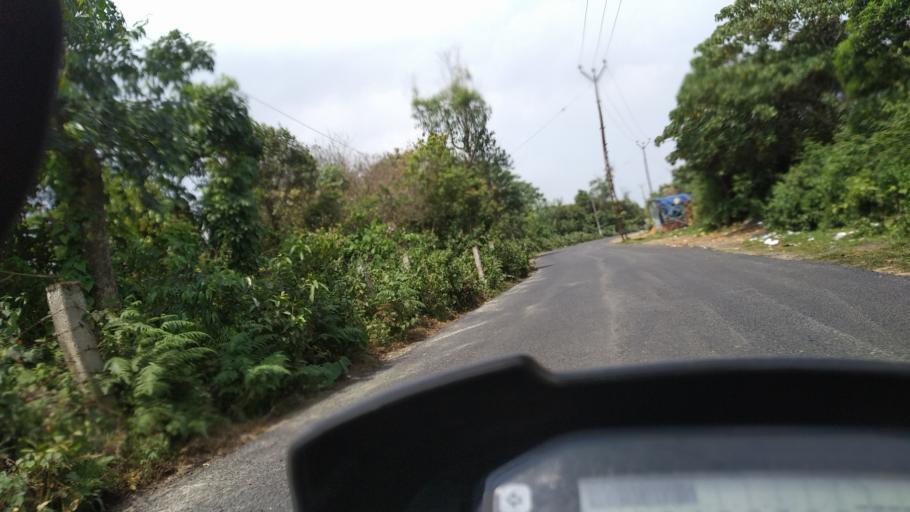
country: IN
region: Kerala
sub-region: Kottayam
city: Erattupetta
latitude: 9.6460
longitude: 76.9271
